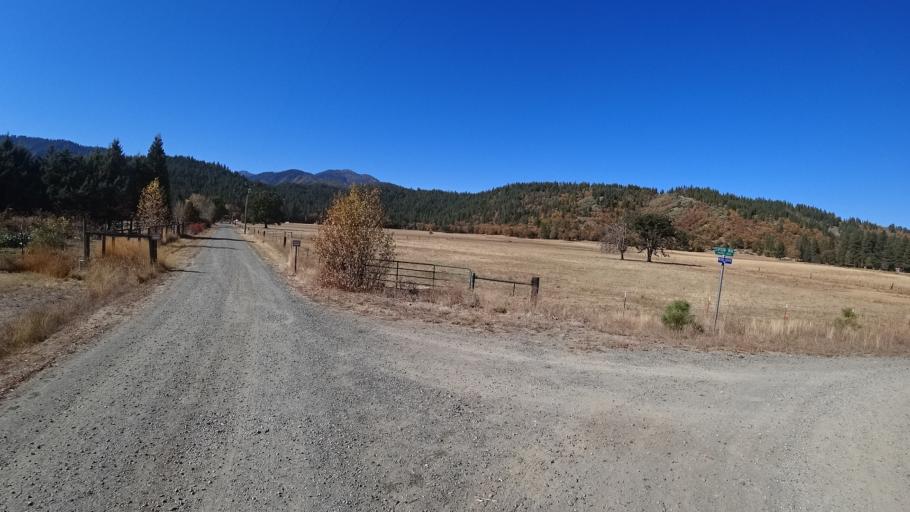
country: US
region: California
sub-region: Siskiyou County
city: Yreka
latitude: 41.5266
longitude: -122.9212
